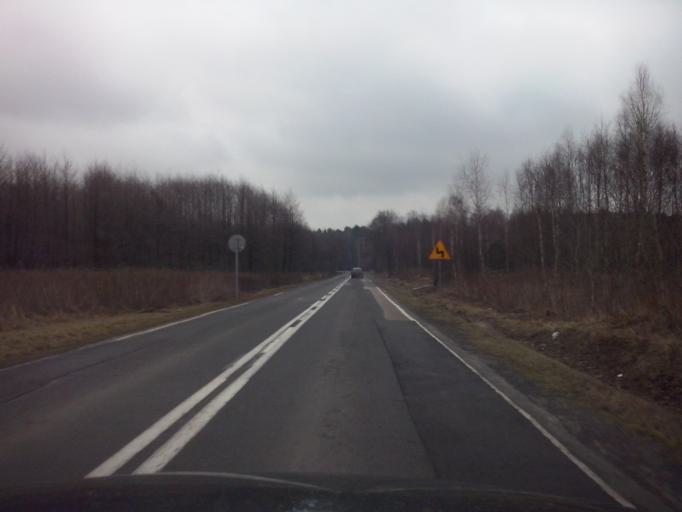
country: PL
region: Subcarpathian Voivodeship
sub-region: Powiat nizanski
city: Przedzel
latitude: 50.5172
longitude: 22.2339
